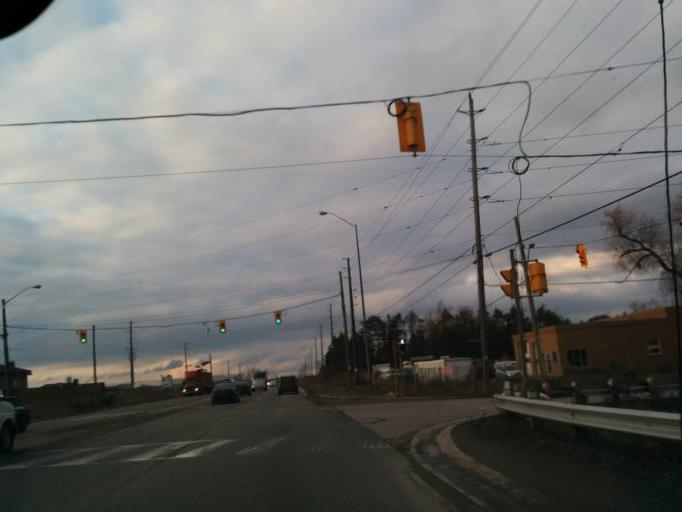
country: CA
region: Ontario
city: Brampton
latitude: 43.8191
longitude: -79.6785
